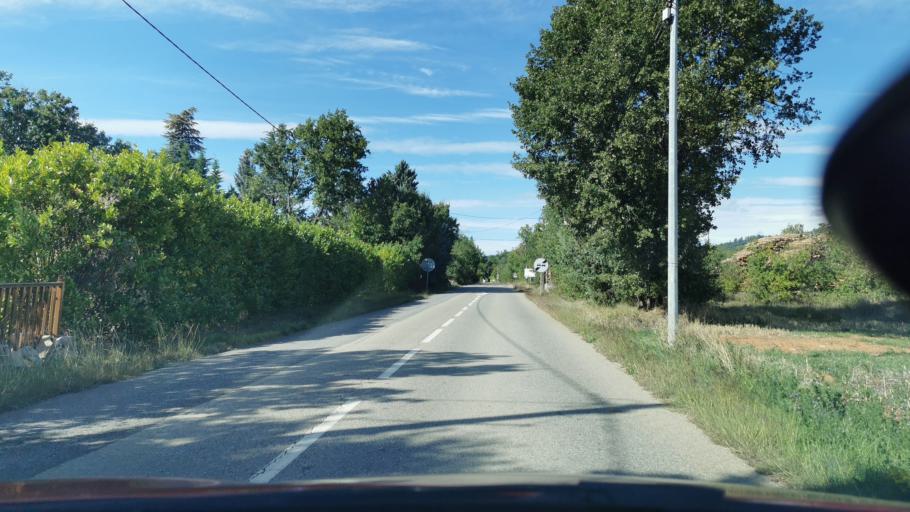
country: FR
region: Provence-Alpes-Cote d'Azur
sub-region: Departement des Alpes-de-Haute-Provence
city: Peipin
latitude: 44.1540
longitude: 5.9741
